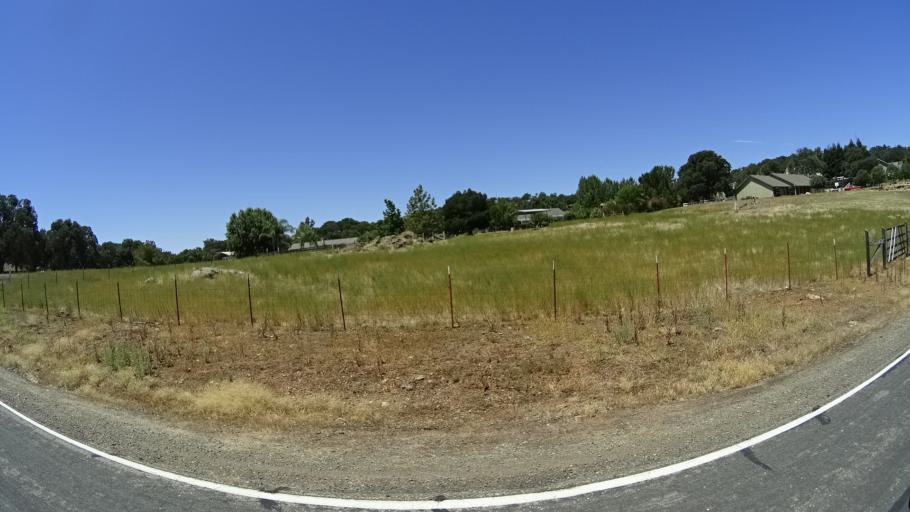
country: US
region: California
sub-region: Calaveras County
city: Rancho Calaveras
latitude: 38.1387
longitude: -120.8364
